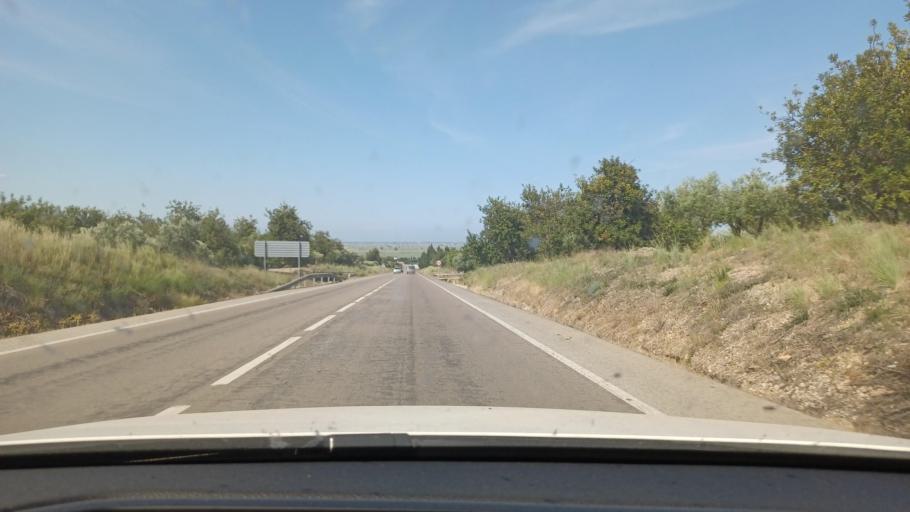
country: ES
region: Catalonia
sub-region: Provincia de Tarragona
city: Sant Carles de la Rapita
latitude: 40.6322
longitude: 0.5841
